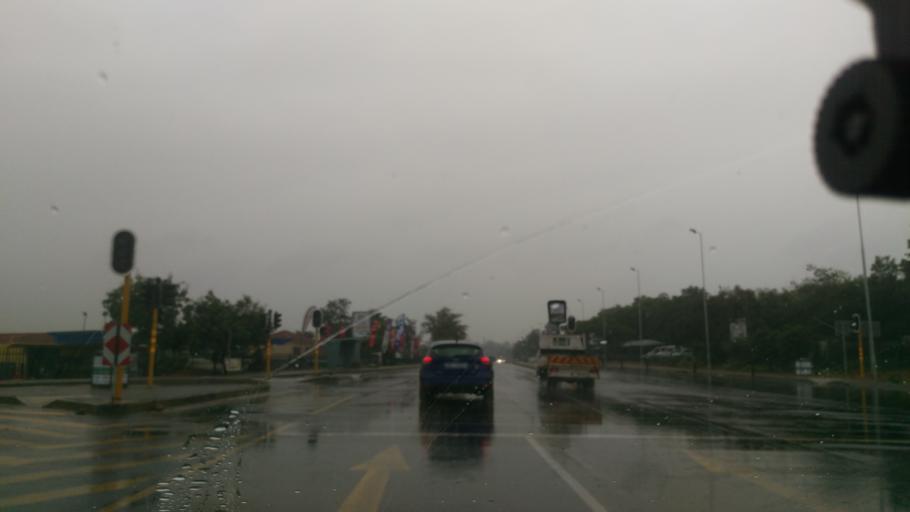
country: ZA
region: Gauteng
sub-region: City of Johannesburg Metropolitan Municipality
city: Diepsloot
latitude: -25.9878
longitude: 27.9846
